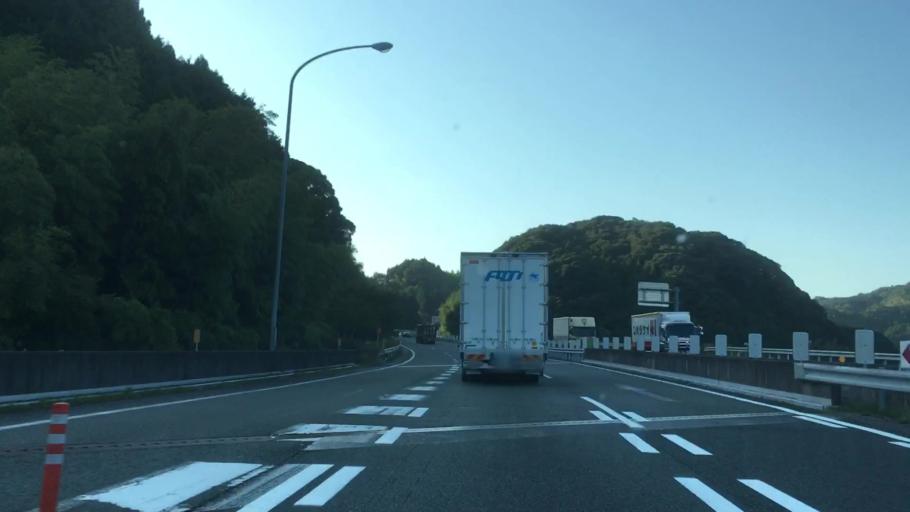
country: JP
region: Yamaguchi
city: Onoda
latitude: 34.1094
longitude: 131.1386
